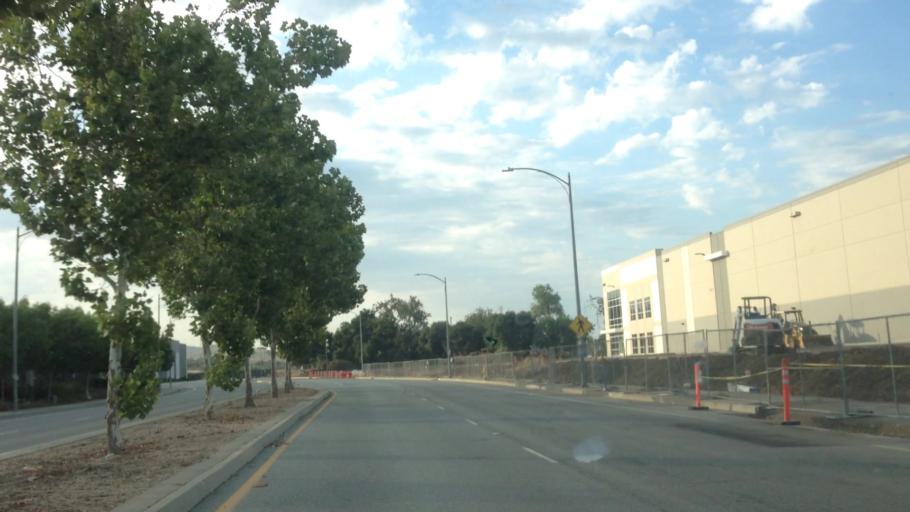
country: US
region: California
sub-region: Santa Clara County
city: Seven Trees
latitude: 37.2573
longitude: -121.7806
